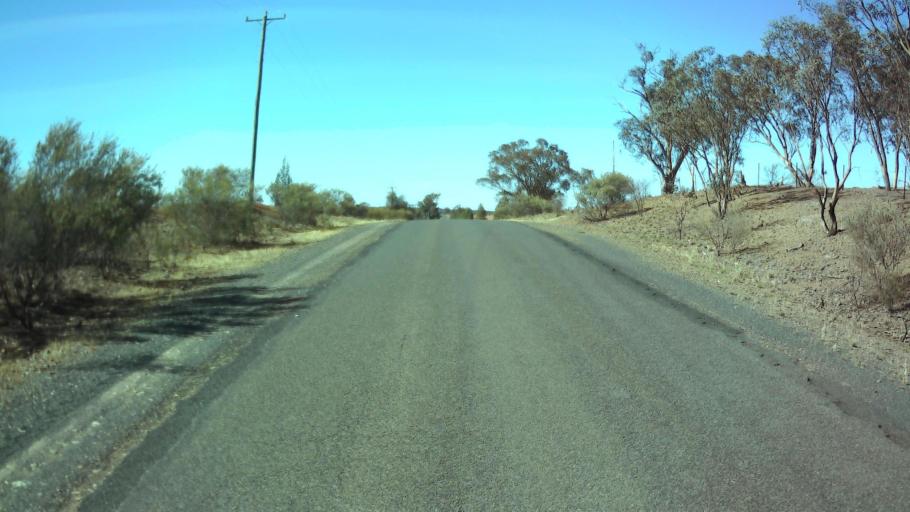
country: AU
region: New South Wales
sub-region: Weddin
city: Grenfell
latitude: -33.7633
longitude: 147.8290
